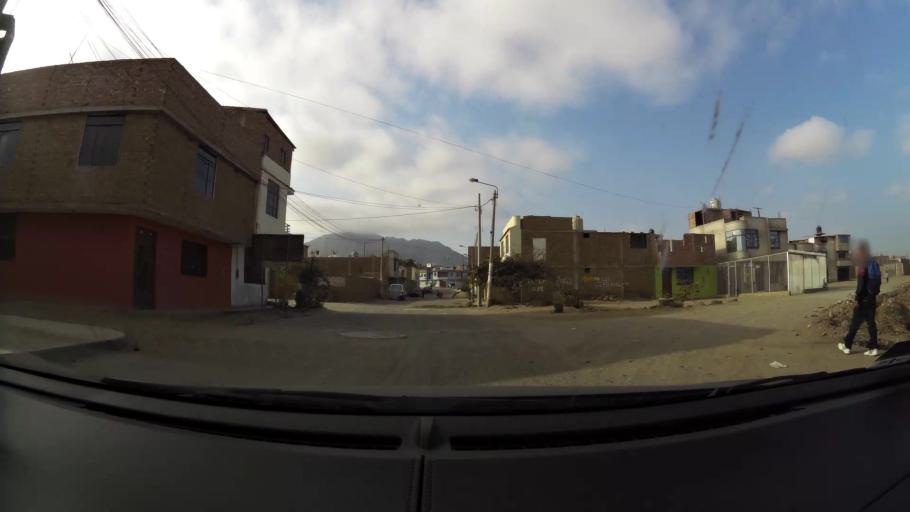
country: PE
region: La Libertad
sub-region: Provincia de Trujillo
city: La Esperanza
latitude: -8.0884
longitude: -79.0362
